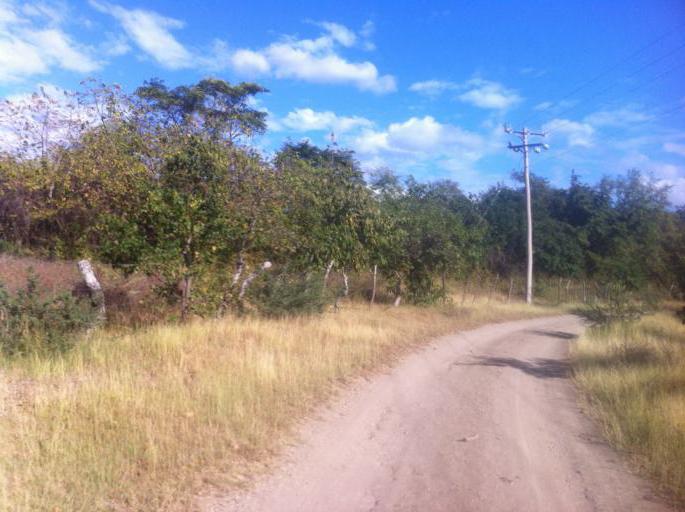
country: NI
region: Managua
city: Carlos Fonseca Amador
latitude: 11.9156
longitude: -86.5961
